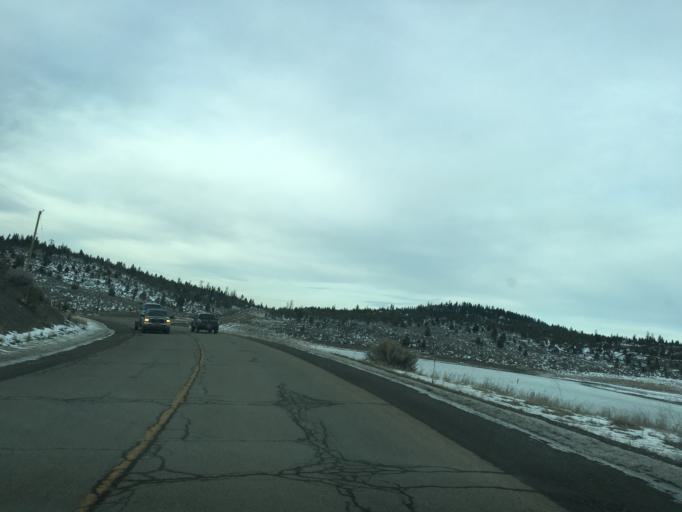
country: CA
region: British Columbia
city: Kamloops
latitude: 50.6292
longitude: -120.4416
